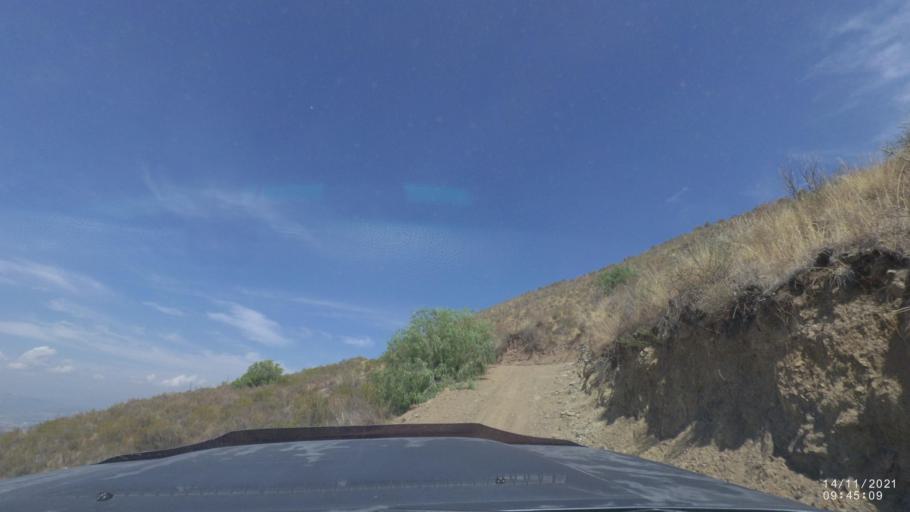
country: BO
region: Cochabamba
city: Cochabamba
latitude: -17.3630
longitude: -66.0873
